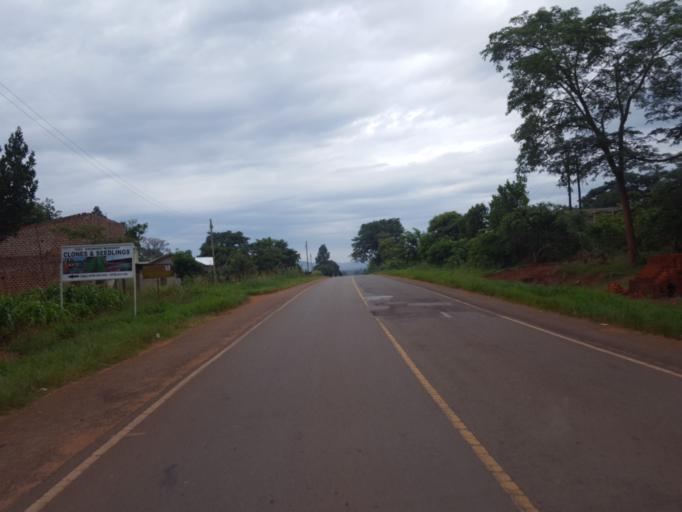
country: UG
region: Central Region
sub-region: Kiboga District
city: Kiboga
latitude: 0.9327
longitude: 31.7553
